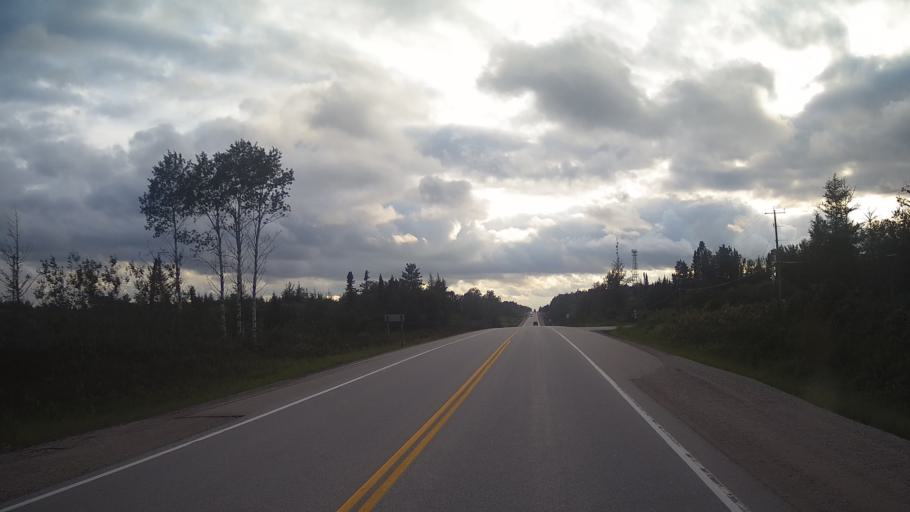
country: CA
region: Ontario
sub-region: Rainy River District
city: Atikokan
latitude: 49.0509
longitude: -90.4893
